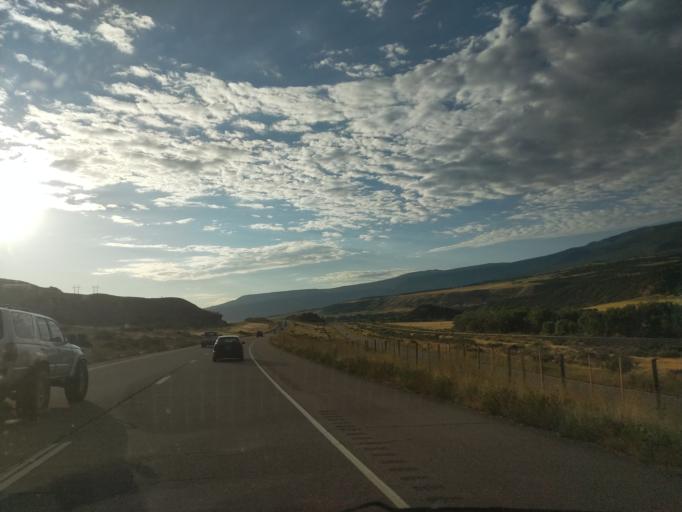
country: US
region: Colorado
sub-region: Garfield County
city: Battlement Mesa
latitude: 39.5008
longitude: -107.9305
